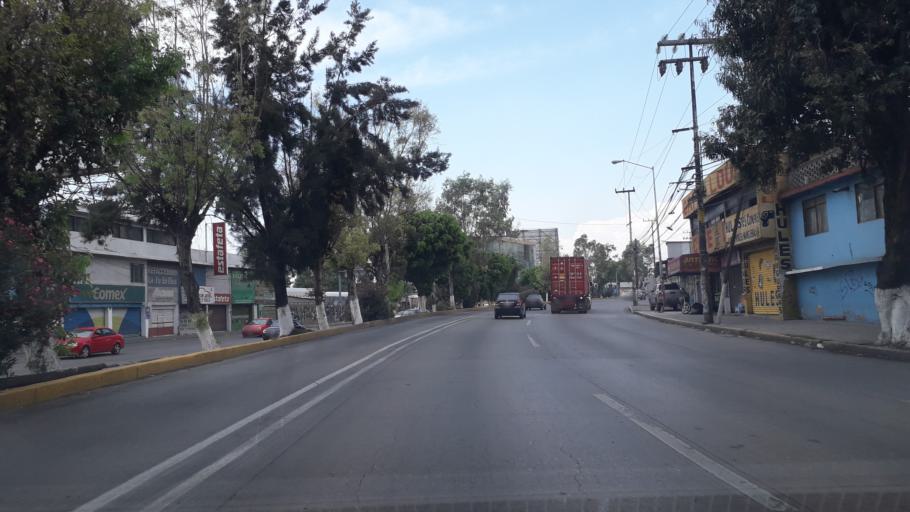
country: MX
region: Mexico
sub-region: Tultitlan
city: Buenavista
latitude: 19.6159
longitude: -99.1804
